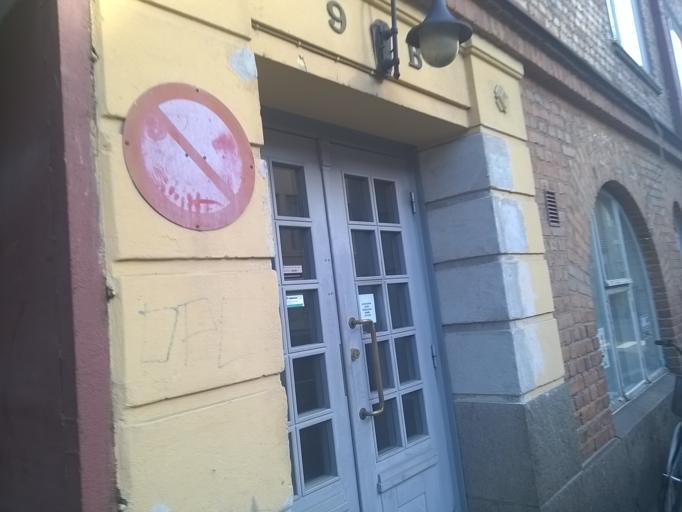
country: FI
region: Pirkanmaa
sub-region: Tampere
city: Tampere
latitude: 61.5019
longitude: 23.7663
